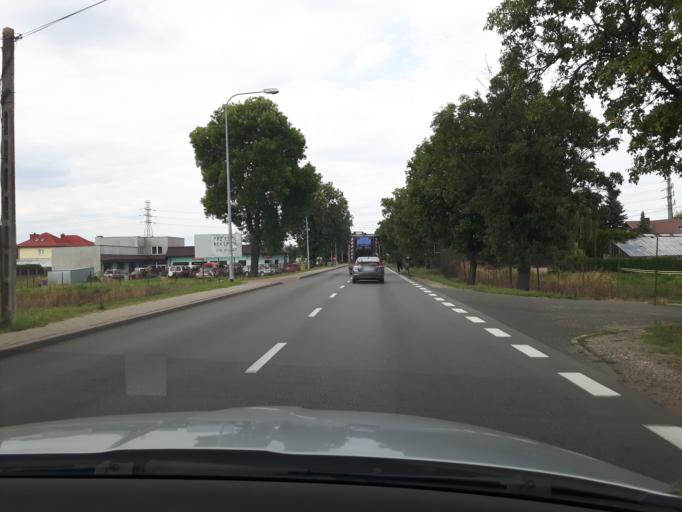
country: PL
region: Masovian Voivodeship
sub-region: Powiat legionowski
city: Stanislawow Pierwszy
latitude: 52.3589
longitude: 21.0289
